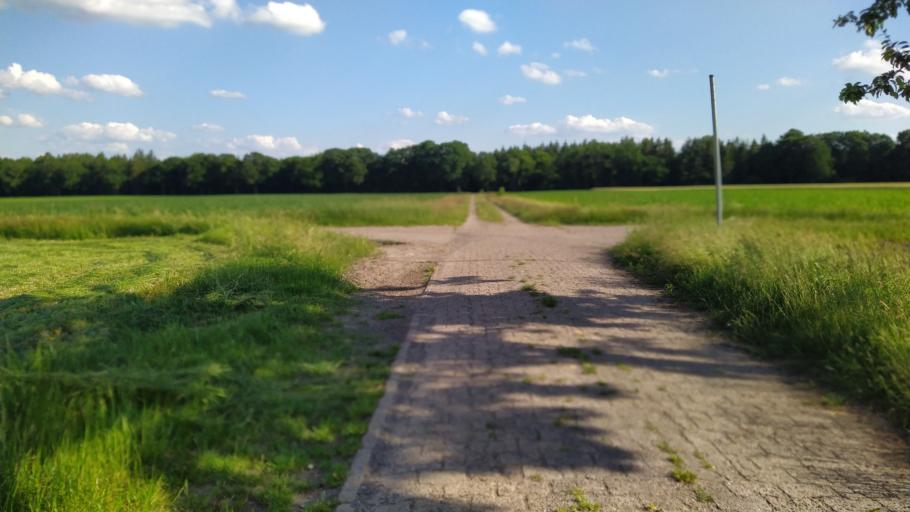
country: DE
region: Lower Saxony
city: Lintig
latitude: 53.6005
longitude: 8.8934
